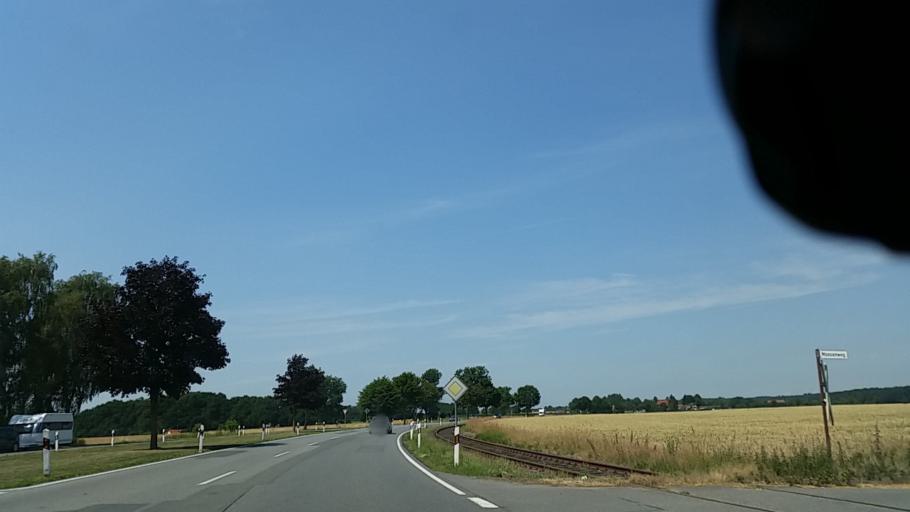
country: DE
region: Lower Saxony
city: Syke
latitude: 52.8876
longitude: 8.8503
